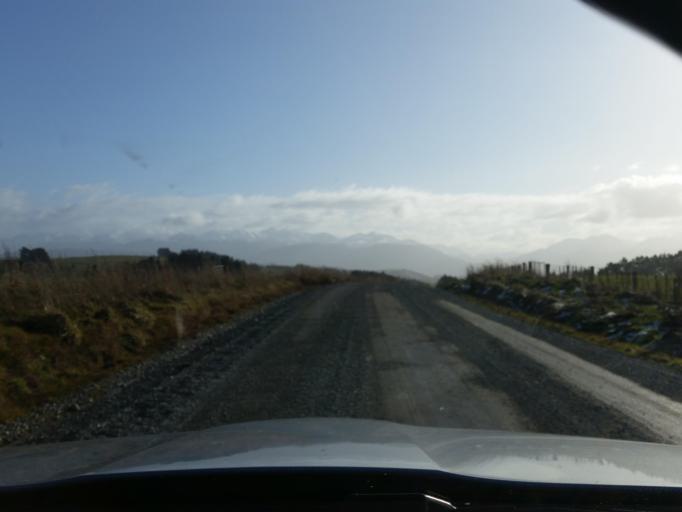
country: NZ
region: Southland
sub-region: Southland District
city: Te Anau
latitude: -45.4646
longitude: 167.8376
